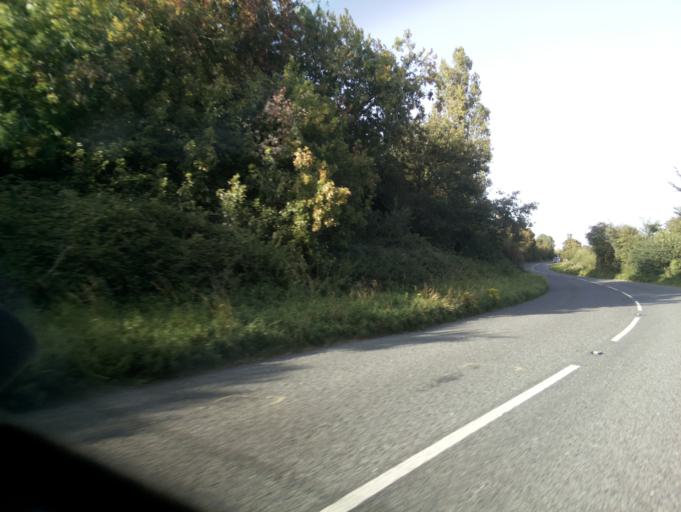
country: GB
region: England
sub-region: Gloucestershire
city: Tewkesbury
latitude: 51.9524
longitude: -2.1927
